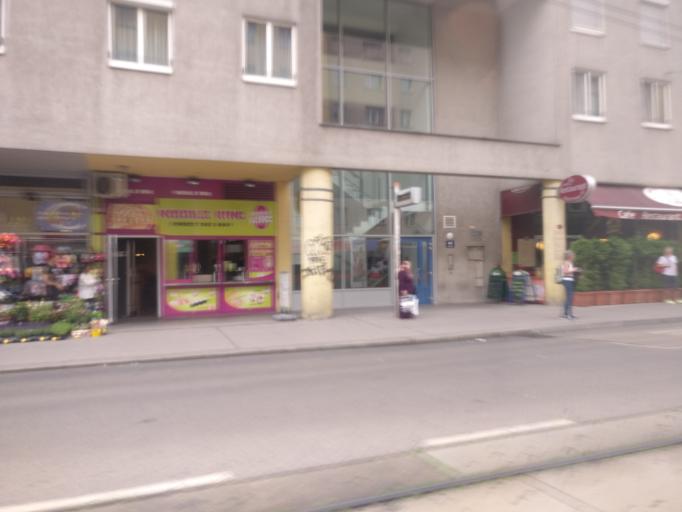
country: AT
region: Vienna
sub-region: Wien Stadt
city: Vienna
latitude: 48.2356
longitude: 16.3703
